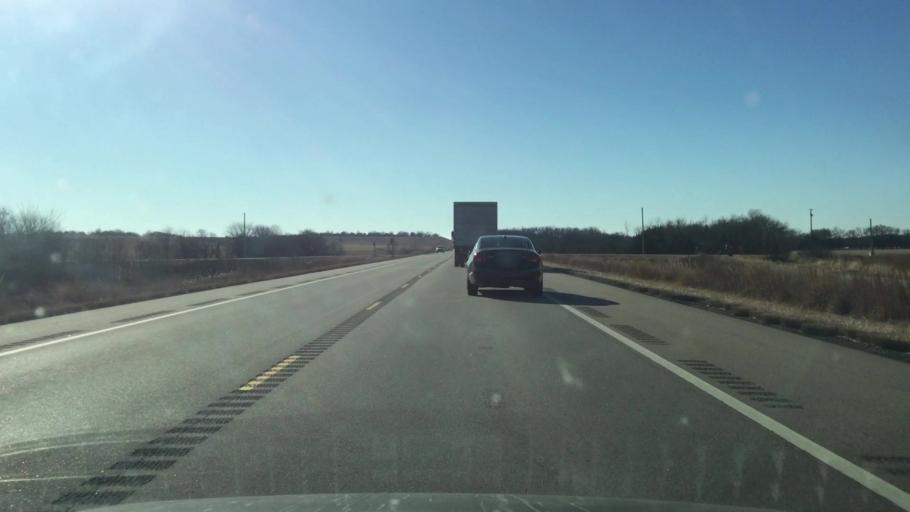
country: US
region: Kansas
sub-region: Allen County
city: Iola
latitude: 38.0259
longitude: -95.3810
